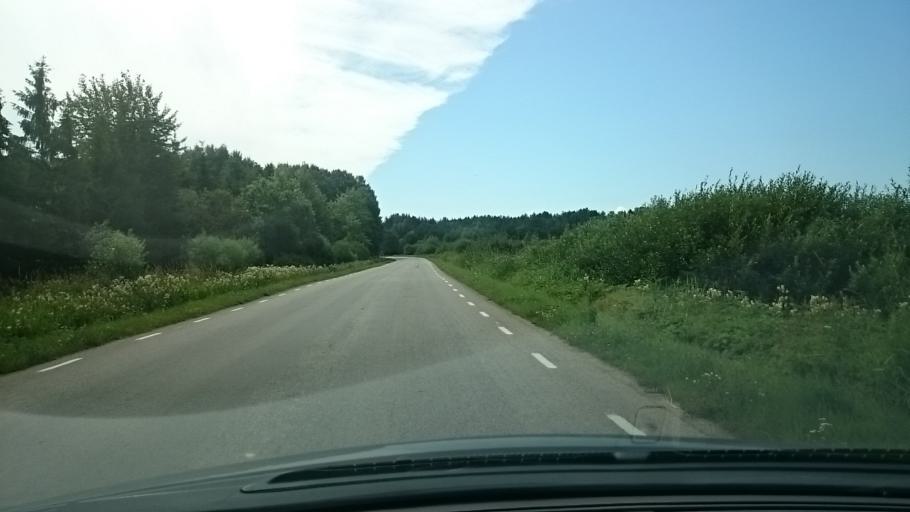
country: EE
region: Laeaene
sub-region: Haapsalu linn
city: Haapsalu
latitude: 59.0317
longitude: 23.5143
